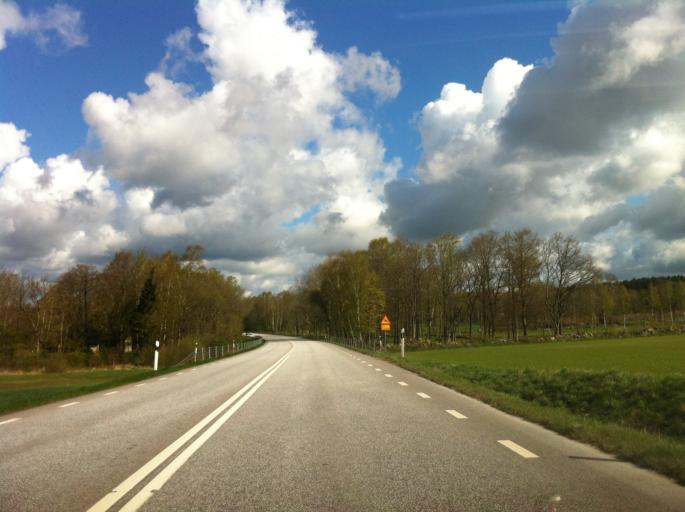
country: SE
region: Skane
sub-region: Horby Kommun
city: Hoerby
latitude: 55.8777
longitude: 13.6316
